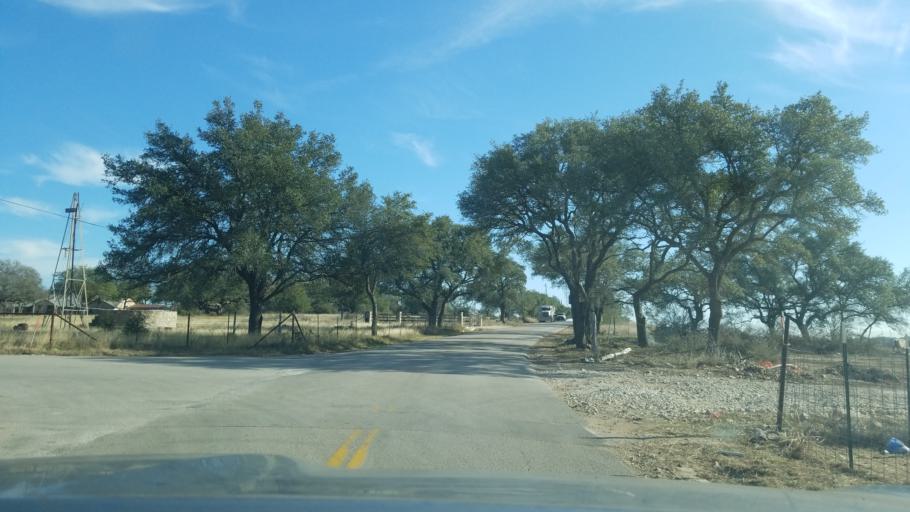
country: US
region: Texas
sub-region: Comal County
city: Canyon Lake
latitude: 29.7874
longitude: -98.2861
